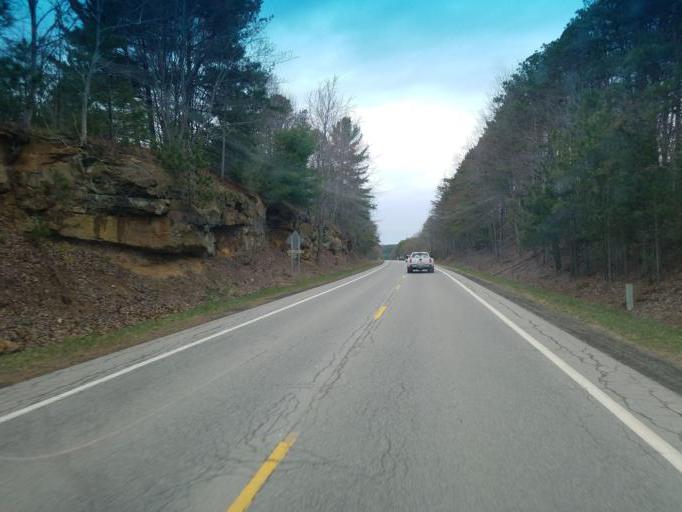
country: US
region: Ohio
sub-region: Ashland County
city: Loudonville
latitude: 40.5747
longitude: -82.2623
